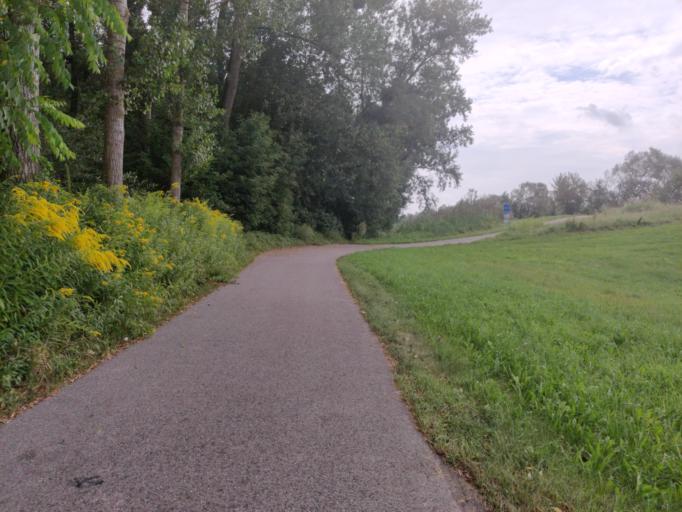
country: AT
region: Upper Austria
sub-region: Politischer Bezirk Perg
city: Perg
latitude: 48.2040
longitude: 14.6059
